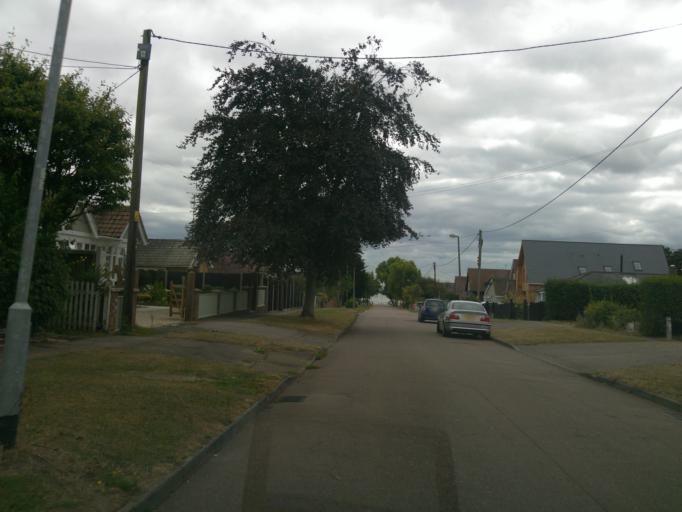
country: GB
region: England
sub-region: Essex
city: West Mersea
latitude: 51.7765
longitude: 0.9303
